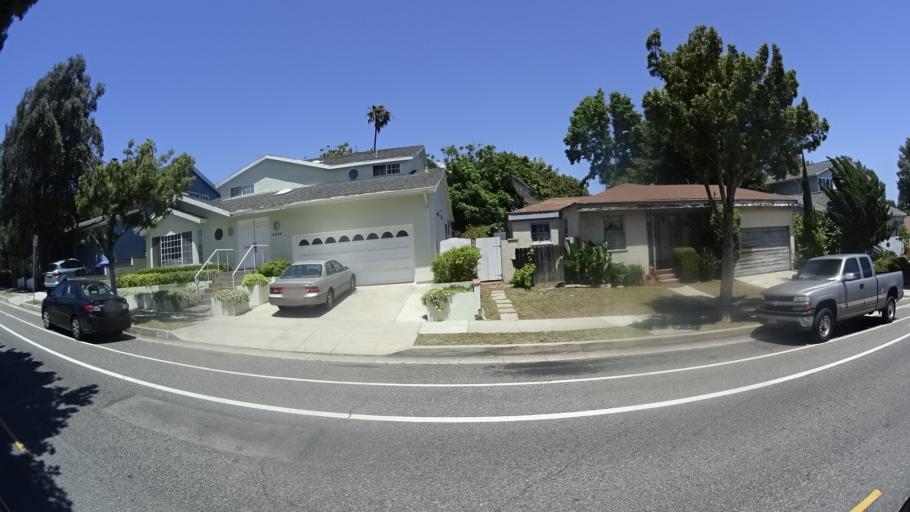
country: US
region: California
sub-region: Los Angeles County
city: Santa Monica
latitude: 34.0073
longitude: -118.4654
